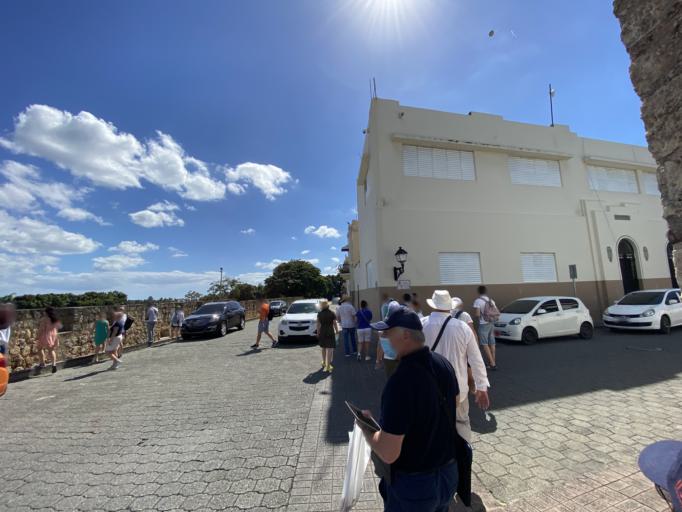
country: DO
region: Nacional
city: Ciudad Nueva
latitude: 18.4727
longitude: -69.8825
